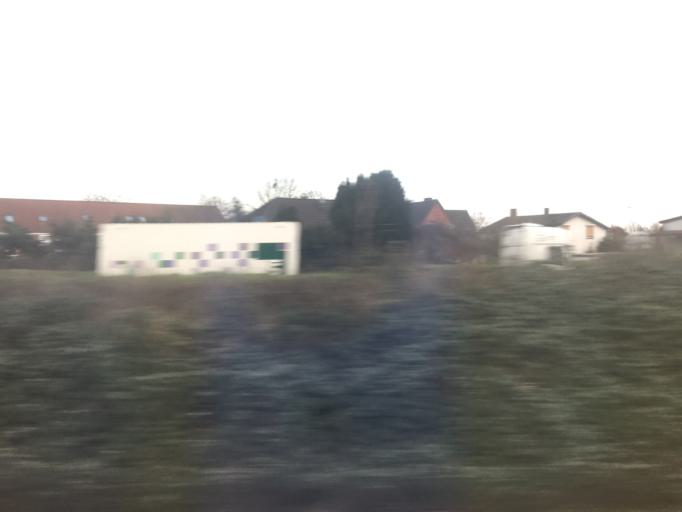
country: DE
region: Schleswig-Holstein
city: Tornesch
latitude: 53.6905
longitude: 9.7258
